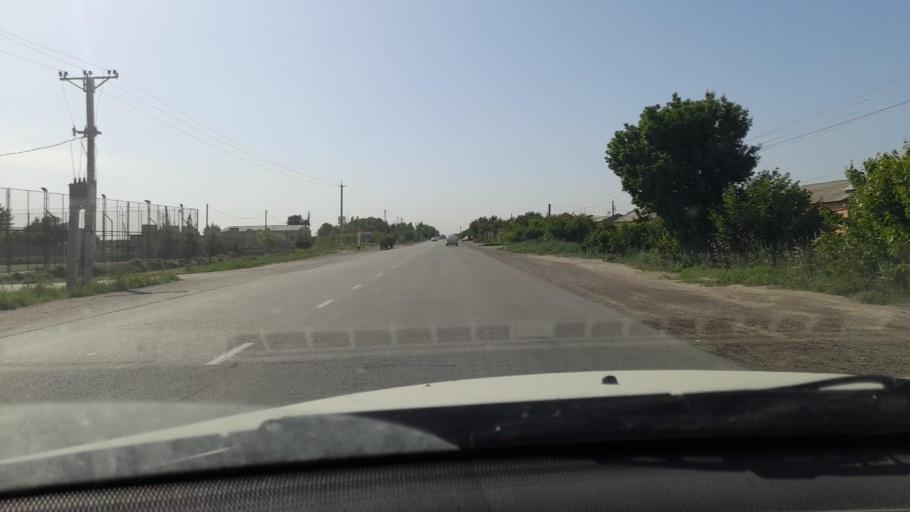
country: UZ
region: Bukhara
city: Romiton
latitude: 39.8998
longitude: 64.4075
